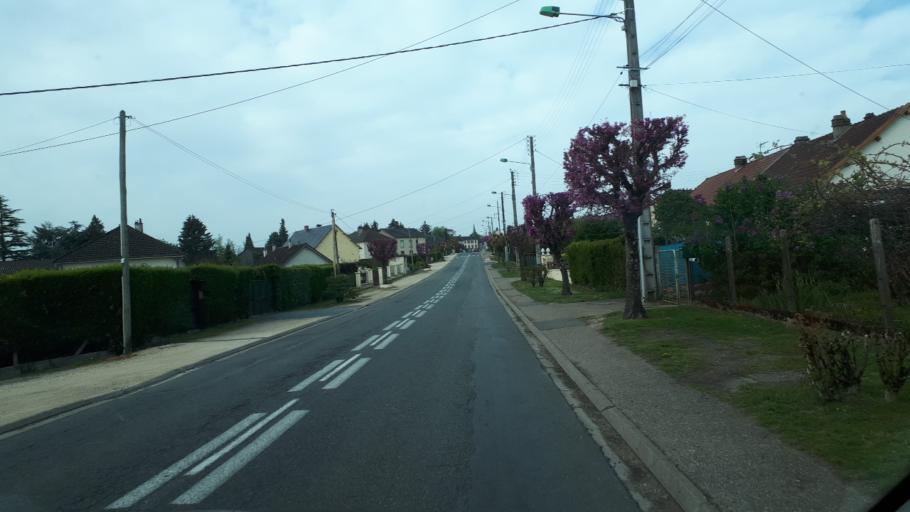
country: FR
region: Centre
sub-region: Departement du Cher
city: Rians
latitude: 47.2015
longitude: 2.5793
